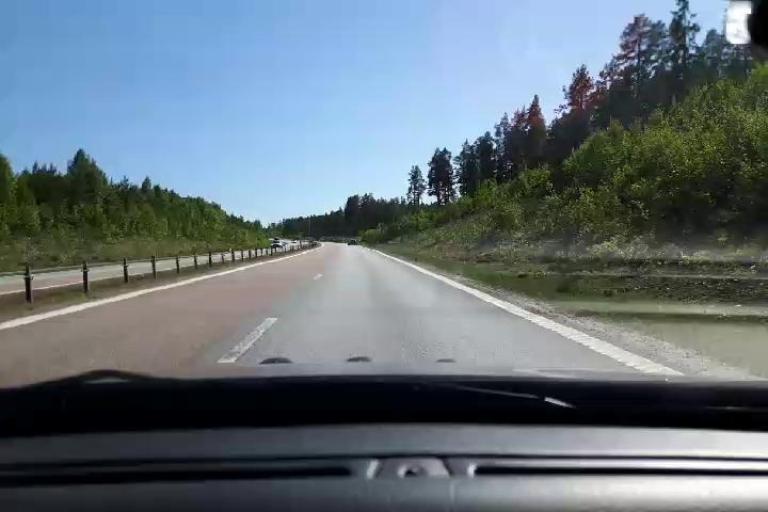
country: SE
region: Gaevleborg
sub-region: Soderhamns Kommun
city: Soderhamn
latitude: 61.4011
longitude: 16.9925
